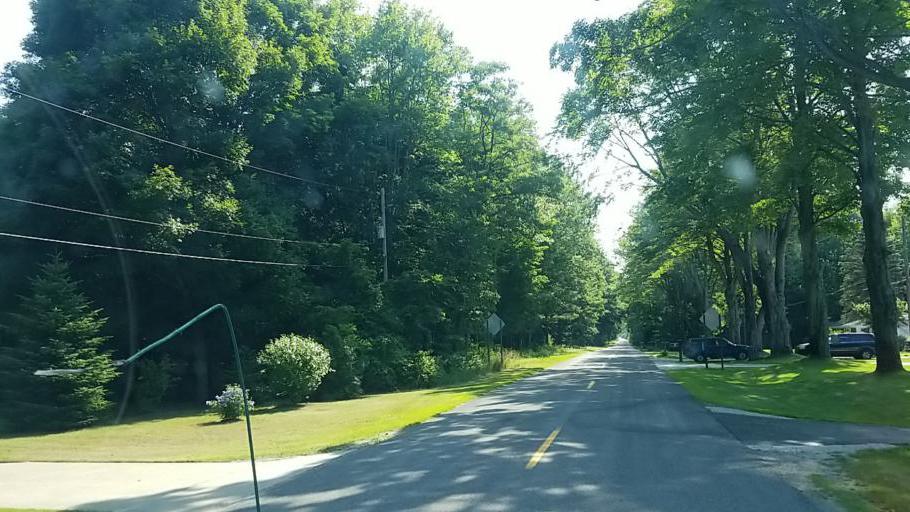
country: US
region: Michigan
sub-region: Muskegon County
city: Whitehall
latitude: 43.3708
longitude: -86.3737
